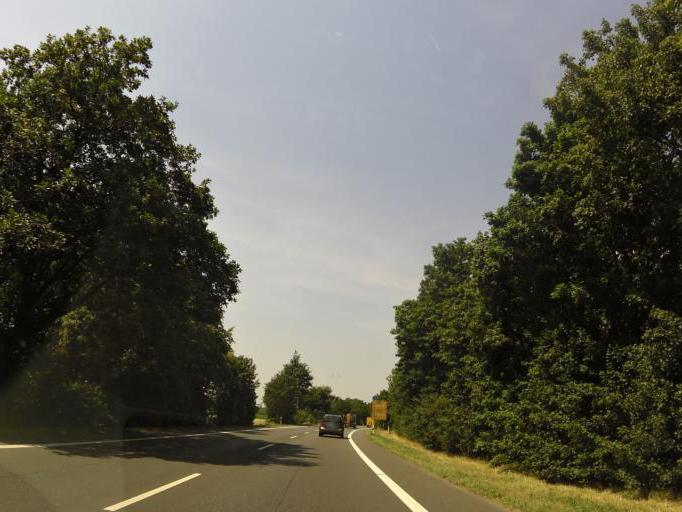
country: DE
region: Hesse
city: Weiterstadt
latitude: 49.9007
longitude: 8.5790
